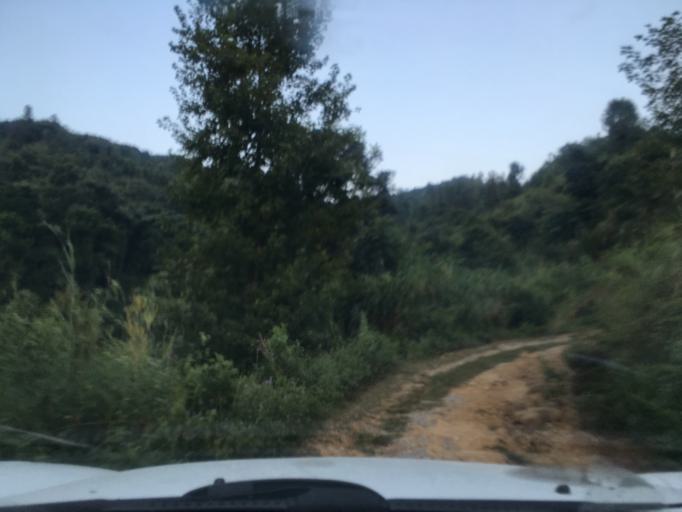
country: CN
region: Guangxi Zhuangzu Zizhiqu
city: Xinzhou
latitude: 25.3514
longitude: 105.7391
